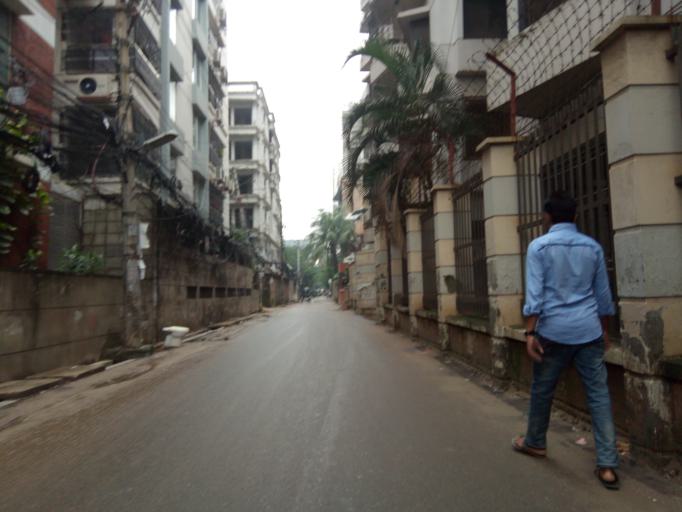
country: BD
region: Dhaka
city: Paltan
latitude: 23.7858
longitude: 90.4003
